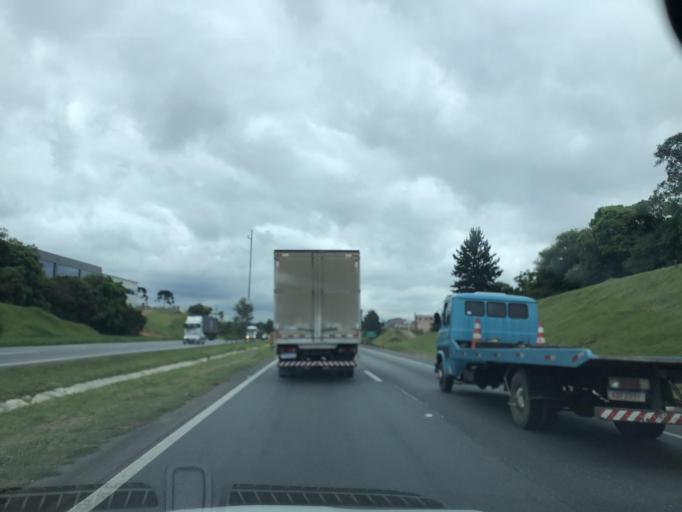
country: BR
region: Parana
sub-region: Sao Jose Dos Pinhais
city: Sao Jose dos Pinhais
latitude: -25.5708
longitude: -49.2121
